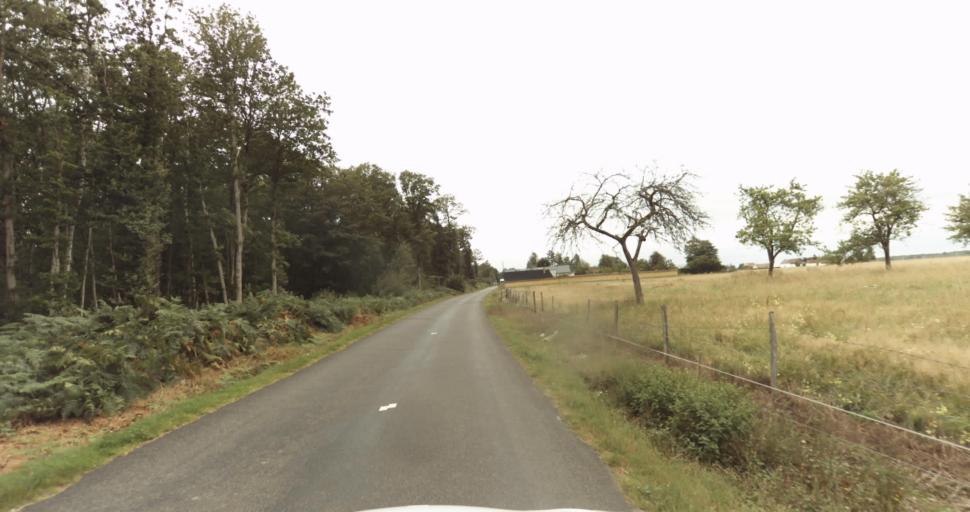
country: FR
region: Haute-Normandie
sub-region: Departement de l'Eure
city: Arnieres-sur-Iton
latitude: 48.9517
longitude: 1.0688
